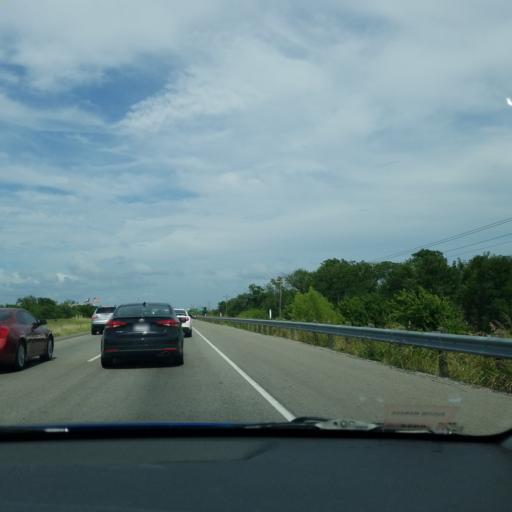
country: US
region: Texas
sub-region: Travis County
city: Manor
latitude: 30.3489
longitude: -97.5512
